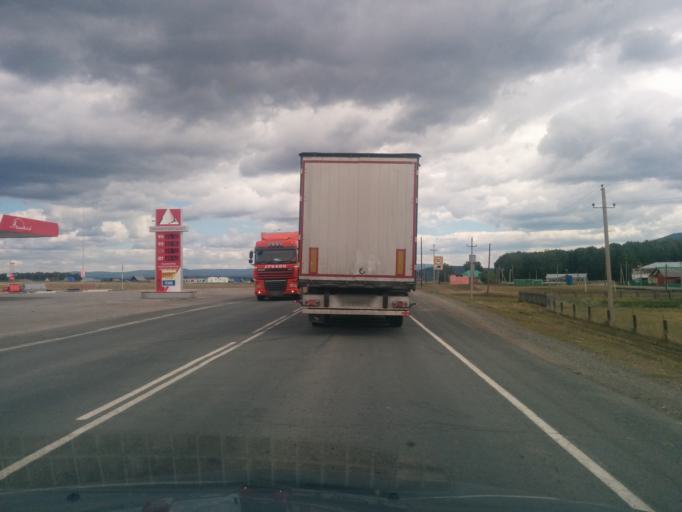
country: RU
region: Bashkortostan
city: Lomovka
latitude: 53.8818
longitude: 58.1038
